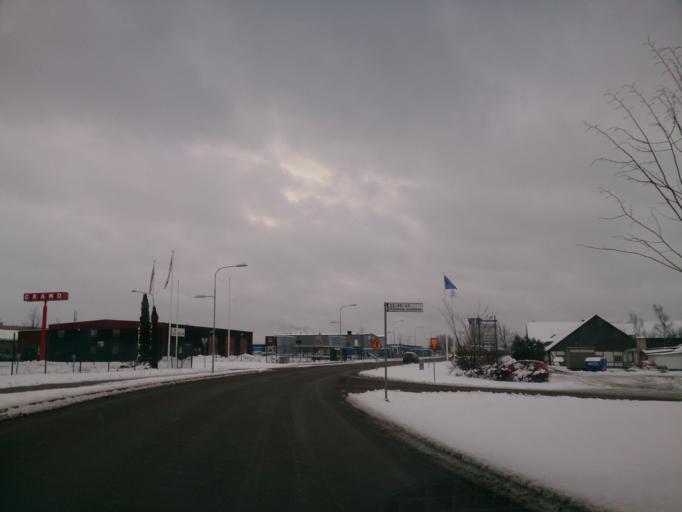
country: SE
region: OEstergoetland
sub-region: Linkopings Kommun
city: Linkoping
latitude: 58.4311
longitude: 15.6122
